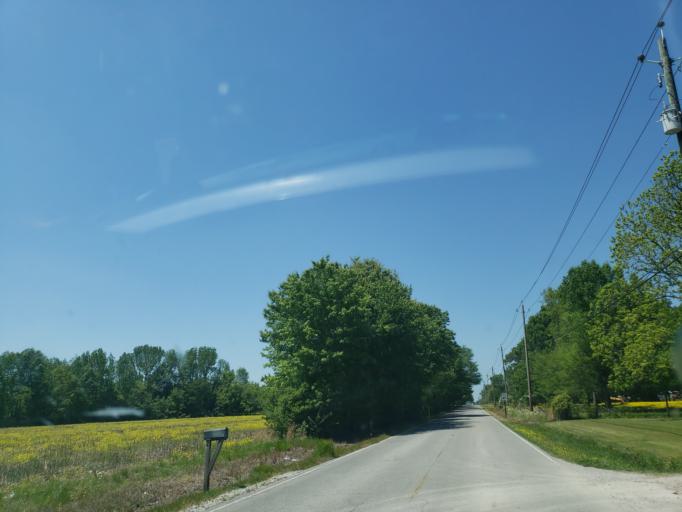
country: US
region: Alabama
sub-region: Madison County
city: Harvest
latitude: 34.9623
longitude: -86.6960
